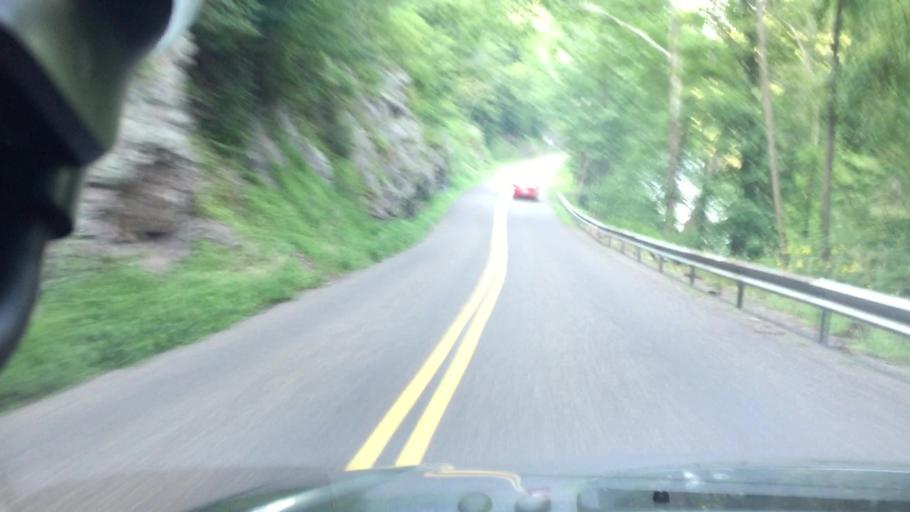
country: US
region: Pennsylvania
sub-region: Columbia County
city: Catawissa
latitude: 40.9663
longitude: -76.4283
